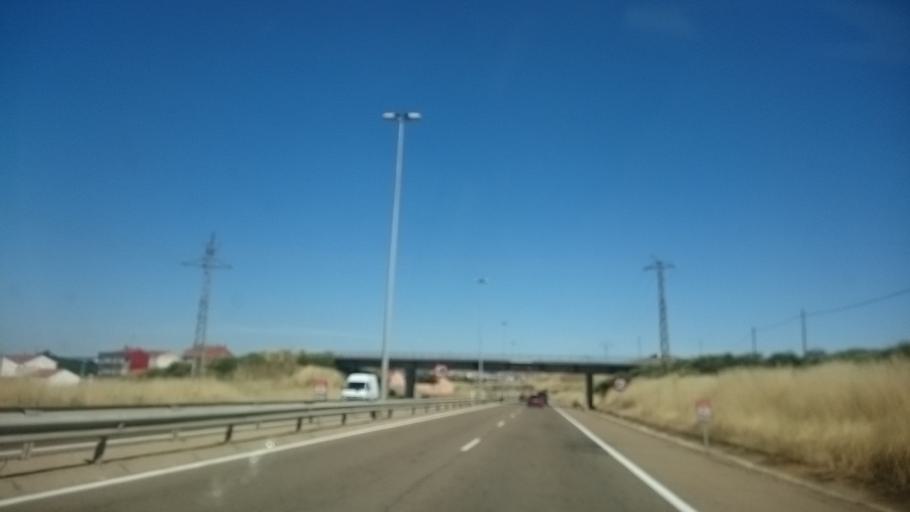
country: ES
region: Castille and Leon
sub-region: Provincia de Leon
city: Leon
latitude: 42.5807
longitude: -5.5461
